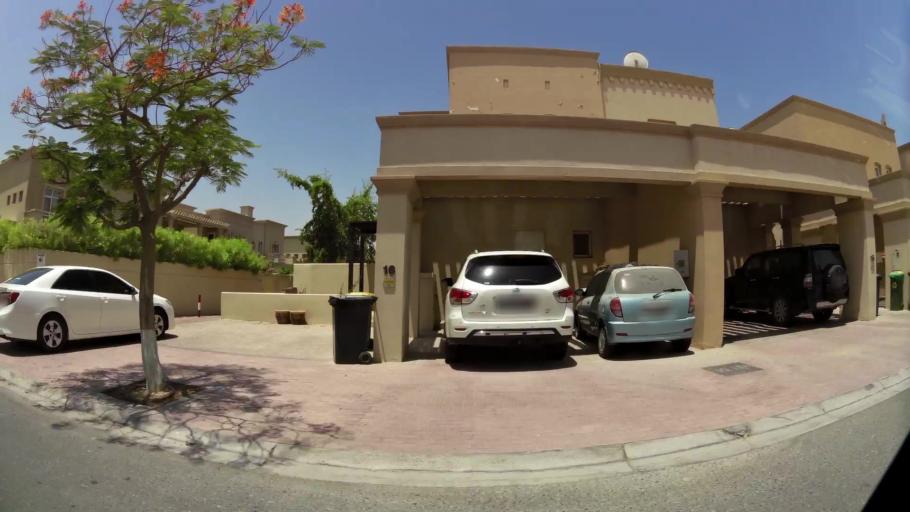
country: AE
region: Dubai
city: Dubai
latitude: 25.0565
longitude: 55.1772
